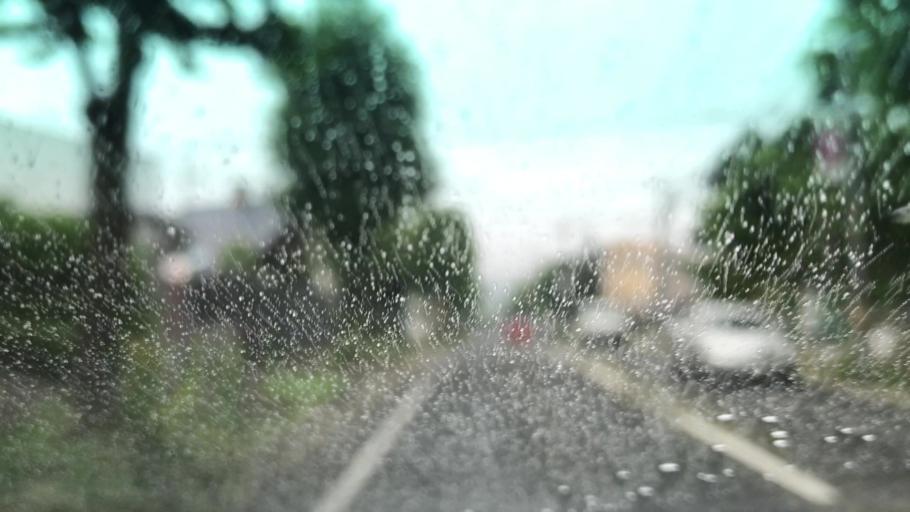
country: JP
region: Hokkaido
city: Sapporo
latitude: 43.0573
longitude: 141.3000
